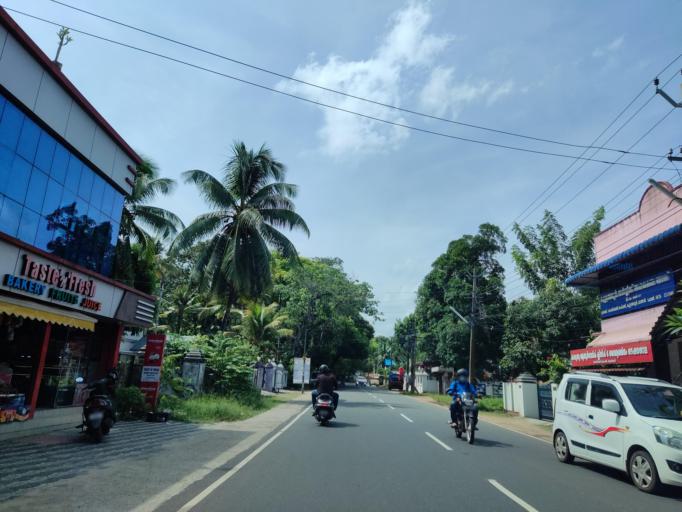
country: IN
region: Kerala
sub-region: Alappuzha
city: Mavelikara
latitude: 9.3008
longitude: 76.5335
